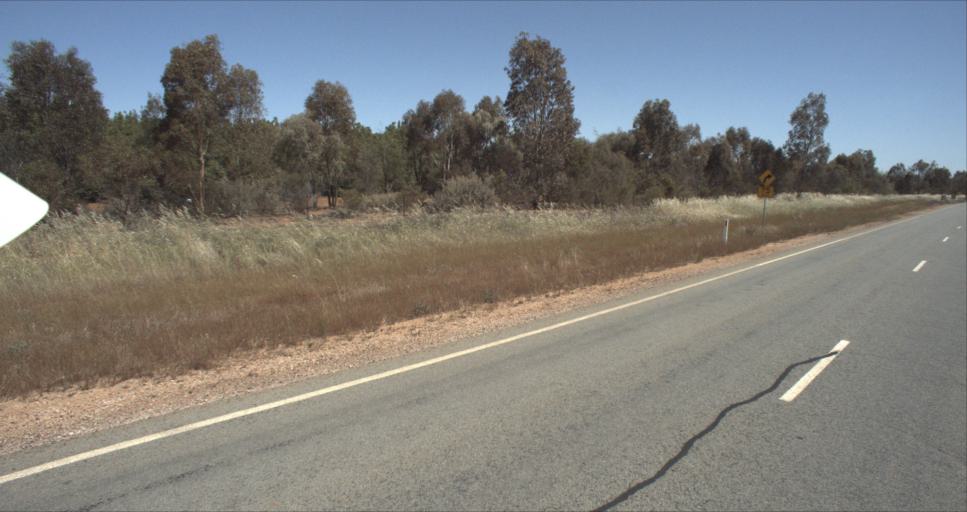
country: AU
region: New South Wales
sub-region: Leeton
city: Leeton
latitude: -34.5036
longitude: 146.4432
